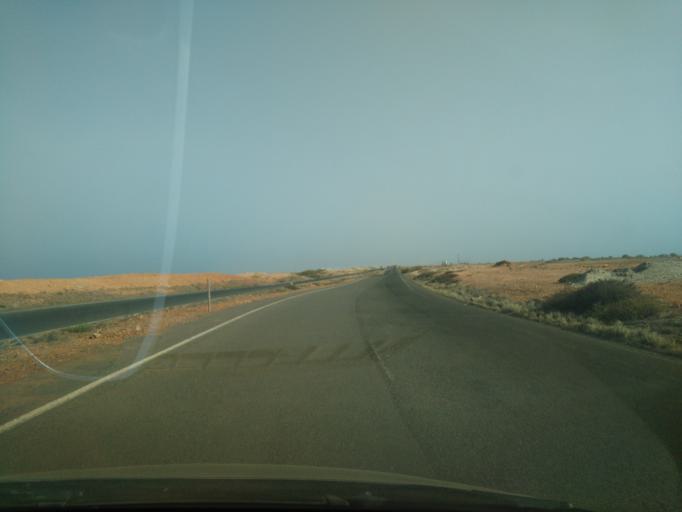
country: CV
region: Sal
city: Santa Maria
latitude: 16.6483
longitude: -22.9181
